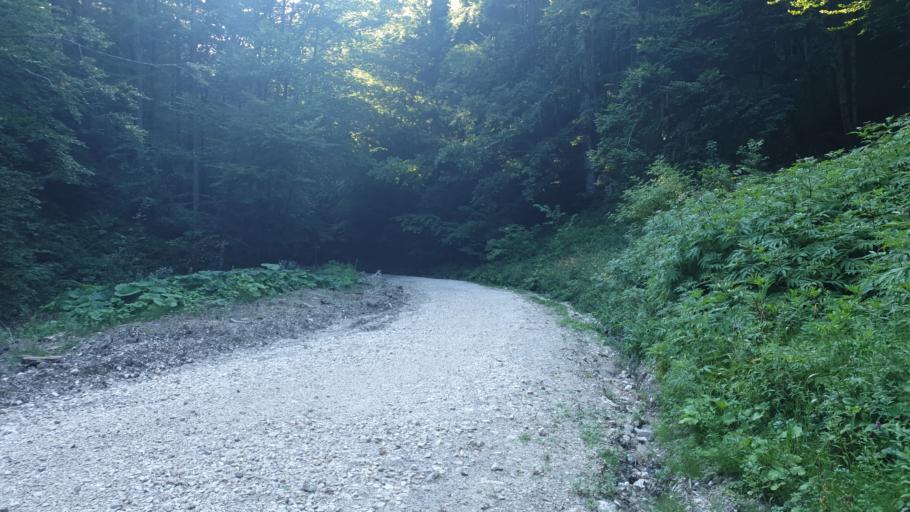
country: RO
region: Brasov
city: Brasov
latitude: 45.6057
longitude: 25.5795
